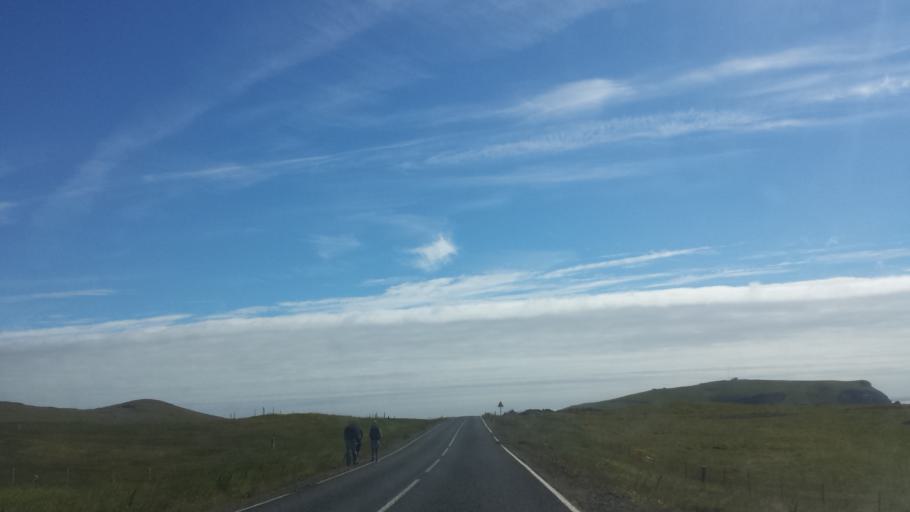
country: IS
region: South
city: Vestmannaeyjar
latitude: 63.4211
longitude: -20.2911
